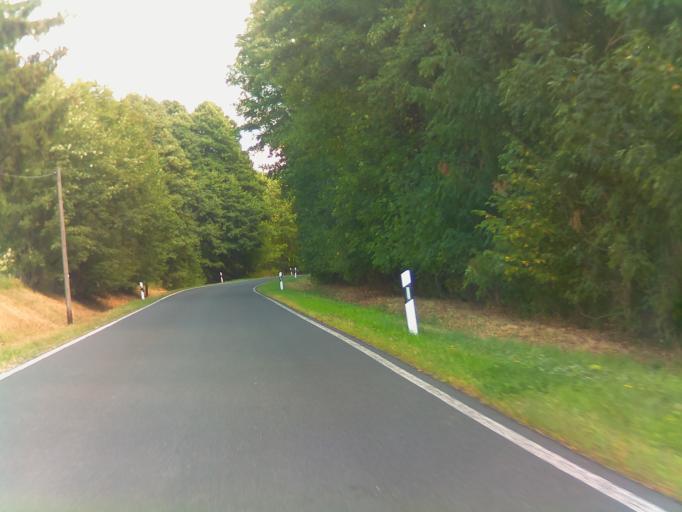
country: DE
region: Bavaria
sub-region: Regierungsbezirk Unterfranken
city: Hausen
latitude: 50.4820
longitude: 10.0875
